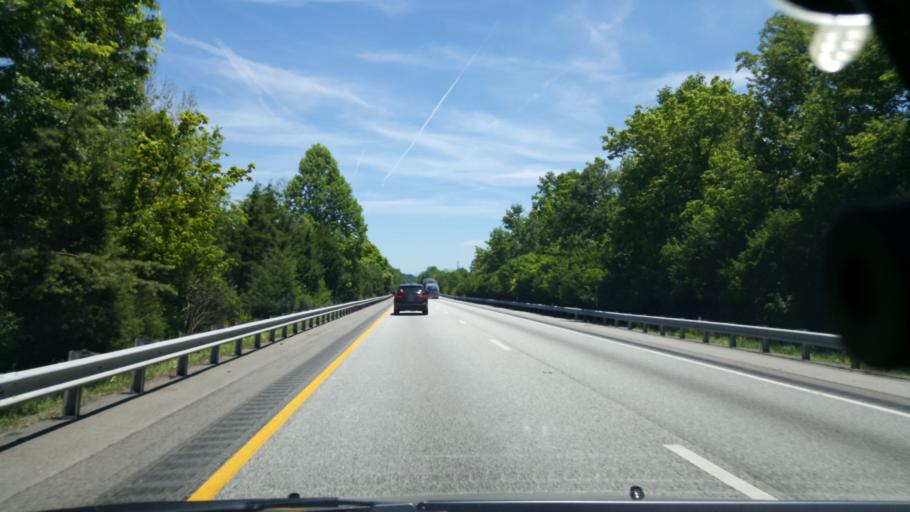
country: US
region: Virginia
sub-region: Botetourt County
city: Fincastle
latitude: 37.4506
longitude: -79.8519
